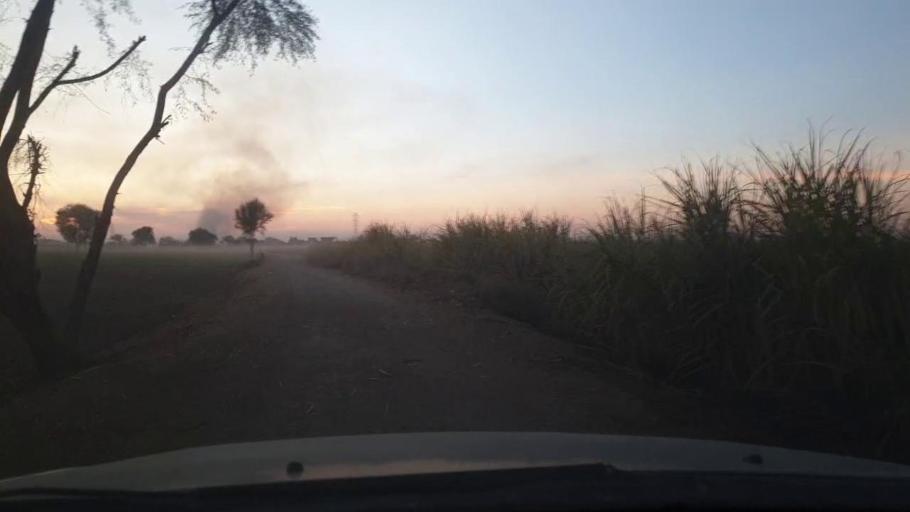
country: PK
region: Sindh
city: Ghotki
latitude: 27.9847
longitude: 69.2696
